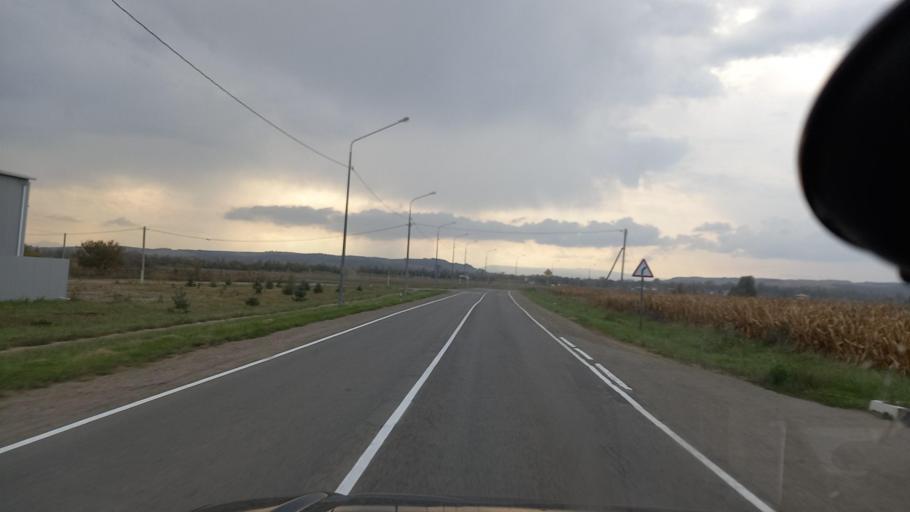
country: RU
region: Krasnodarskiy
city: Mostovskoy
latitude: 44.3936
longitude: 40.7678
